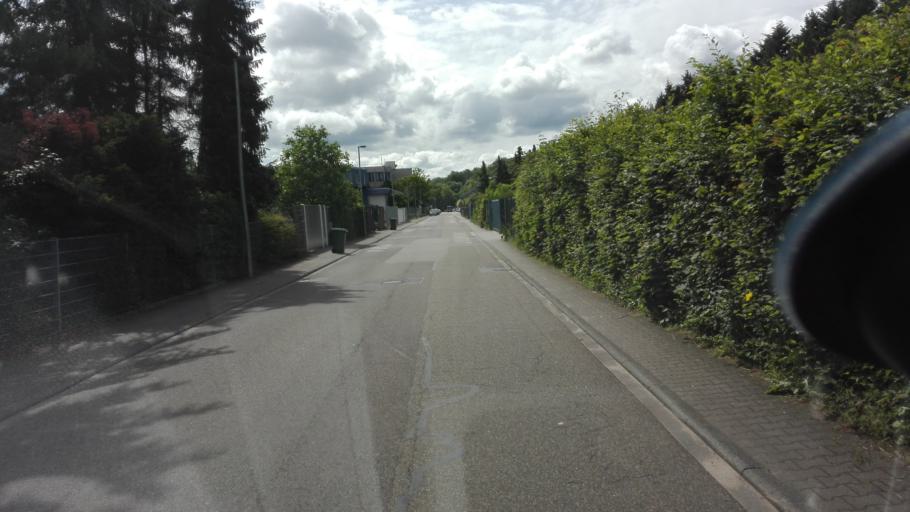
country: DE
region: Baden-Wuerttemberg
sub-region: Karlsruhe Region
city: Walldorf
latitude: 49.2894
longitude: 8.6424
